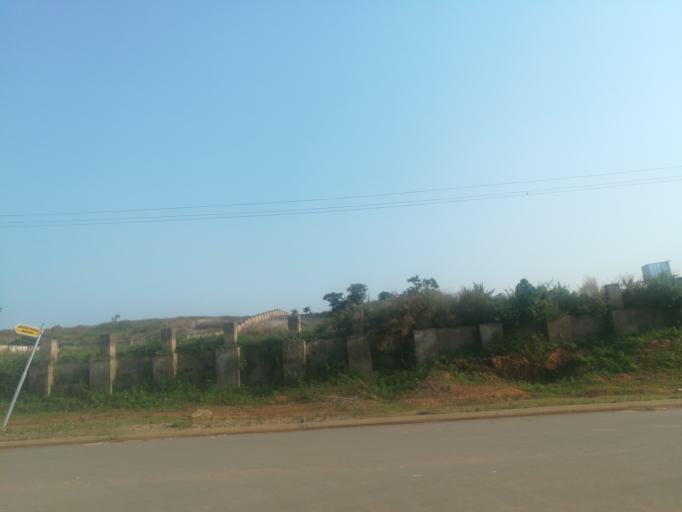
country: NG
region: Abuja Federal Capital Territory
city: Abuja
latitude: 9.0443
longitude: 7.4333
